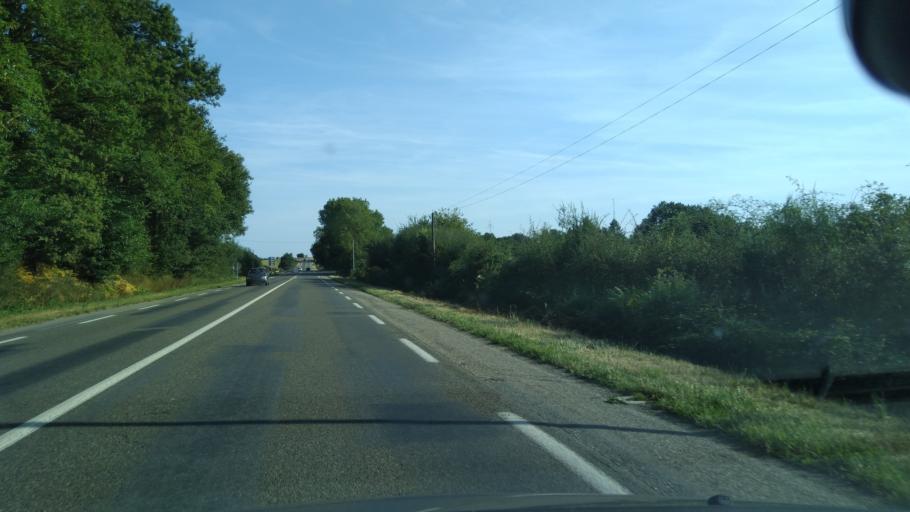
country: FR
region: Pays de la Loire
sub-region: Departement de la Mayenne
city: Entrammes
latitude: 48.0220
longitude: -0.7333
